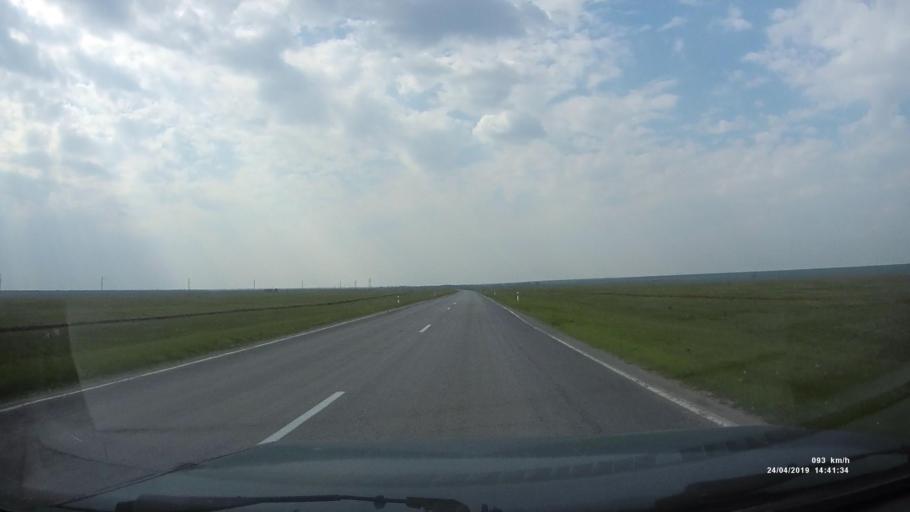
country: RU
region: Rostov
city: Remontnoye
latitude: 46.4461
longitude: 43.8779
